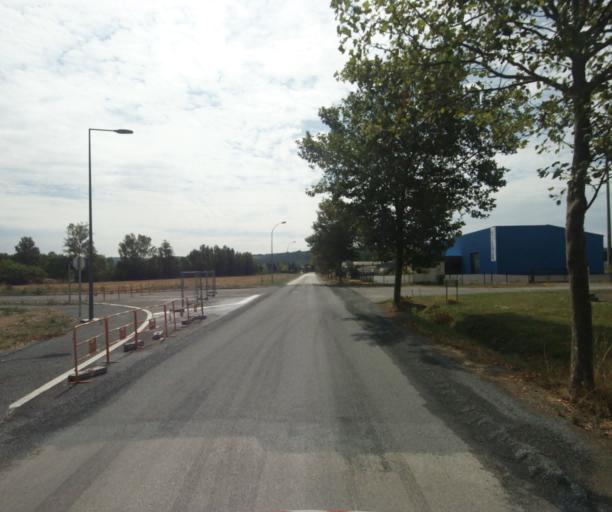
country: FR
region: Midi-Pyrenees
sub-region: Departement de la Haute-Garonne
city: Revel
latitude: 43.4573
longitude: 1.9844
